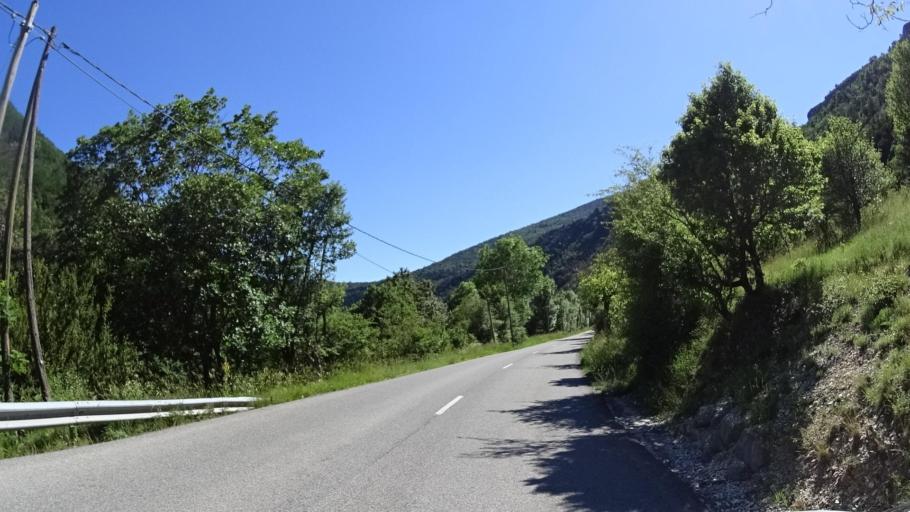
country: FR
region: Provence-Alpes-Cote d'Azur
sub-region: Departement des Alpes-de-Haute-Provence
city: Annot
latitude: 44.0330
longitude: 6.5595
